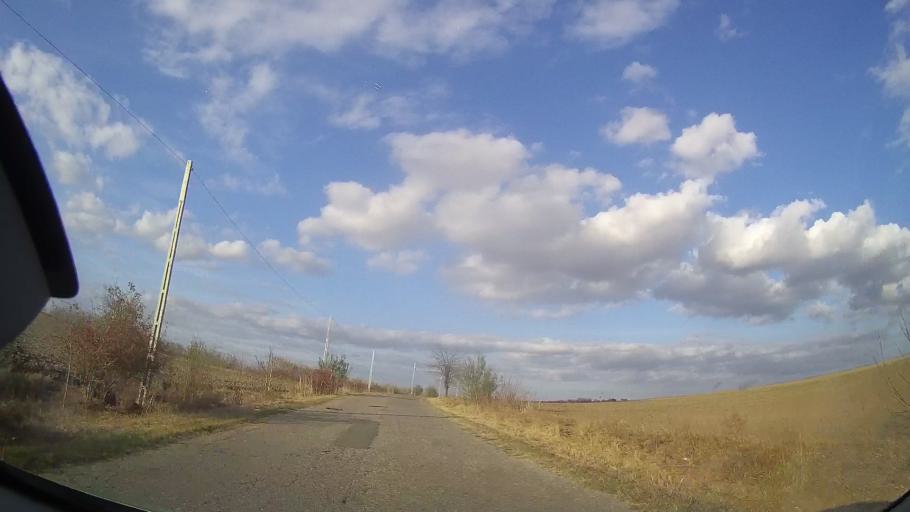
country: RO
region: Constanta
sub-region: Comuna Cerchezu
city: Cerchezu
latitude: 43.8453
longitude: 28.0985
